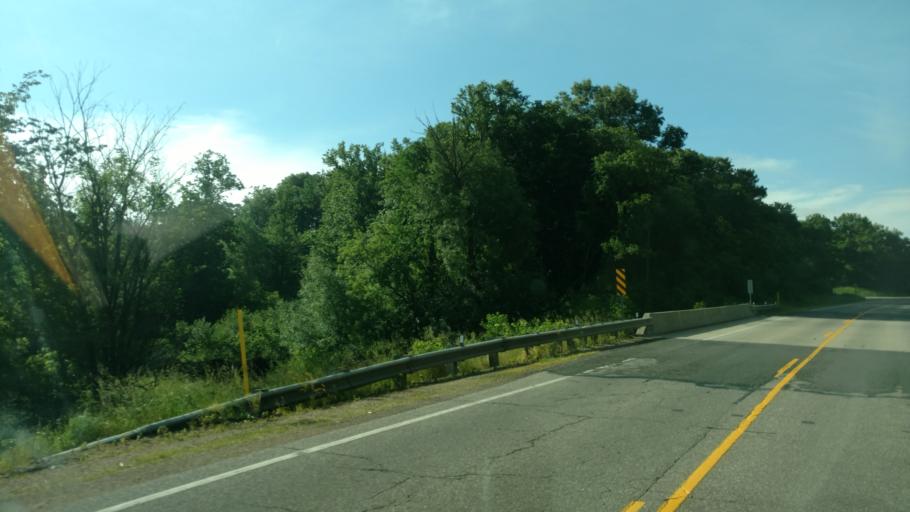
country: US
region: Wisconsin
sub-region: Sauk County
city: Reedsburg
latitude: 43.5724
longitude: -90.1329
